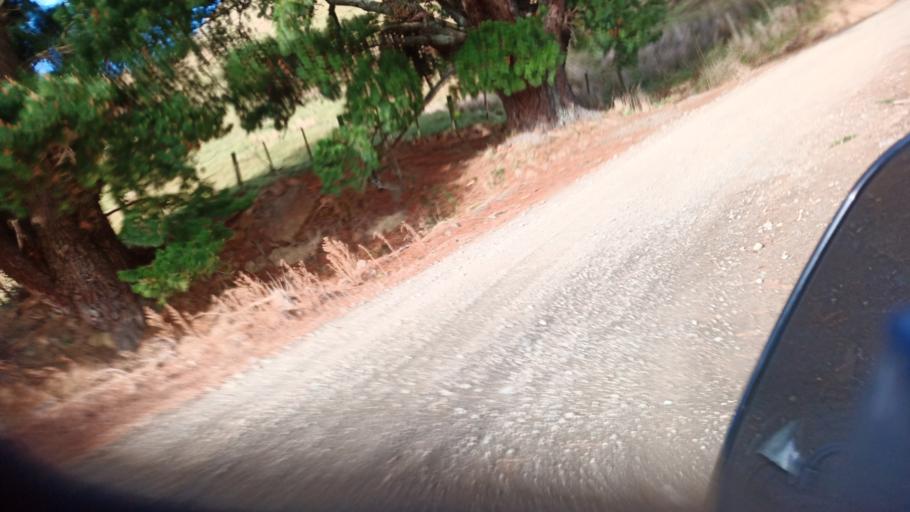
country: NZ
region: Bay of Plenty
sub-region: Opotiki District
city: Opotiki
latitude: -38.4461
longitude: 177.5399
